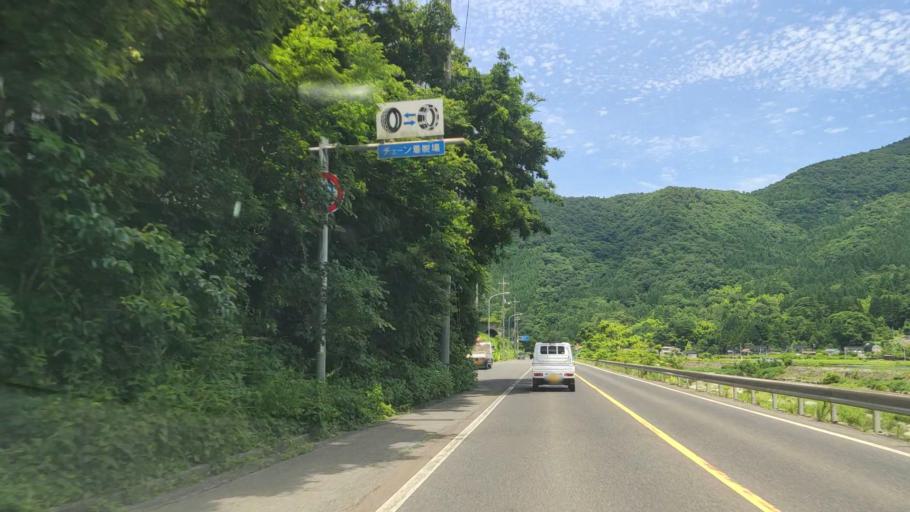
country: JP
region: Tottori
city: Tottori
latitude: 35.3636
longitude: 134.3781
